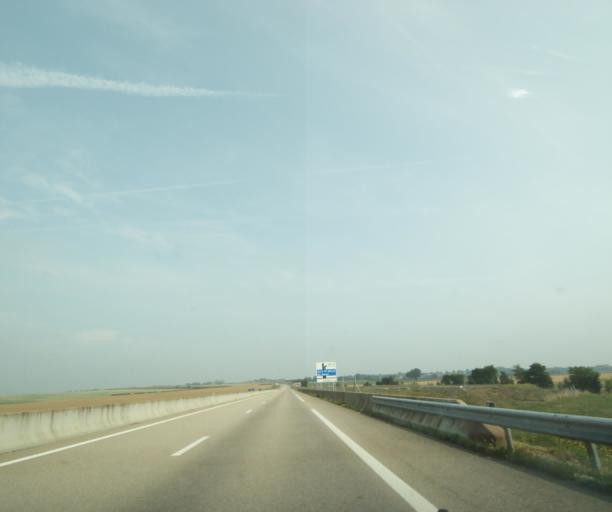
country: FR
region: Lower Normandy
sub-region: Departement de l'Orne
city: Courteilles
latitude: 48.7971
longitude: -0.1264
